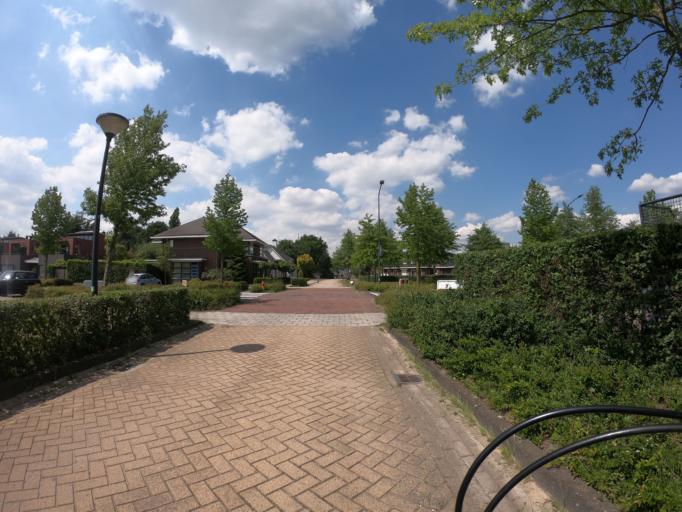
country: NL
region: North Brabant
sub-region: Gemeente Uden
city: Uden
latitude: 51.6454
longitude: 5.6190
